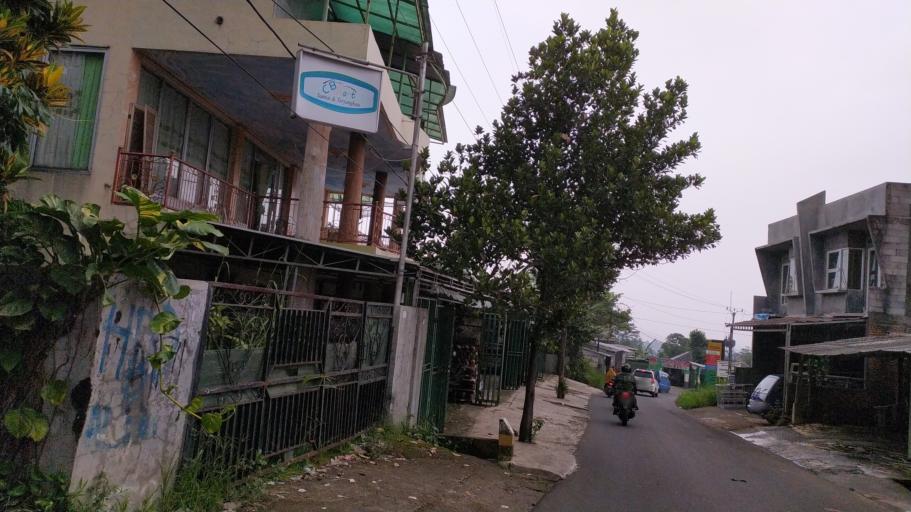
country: ID
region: West Java
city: Ciampea
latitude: -6.6073
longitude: 106.6994
